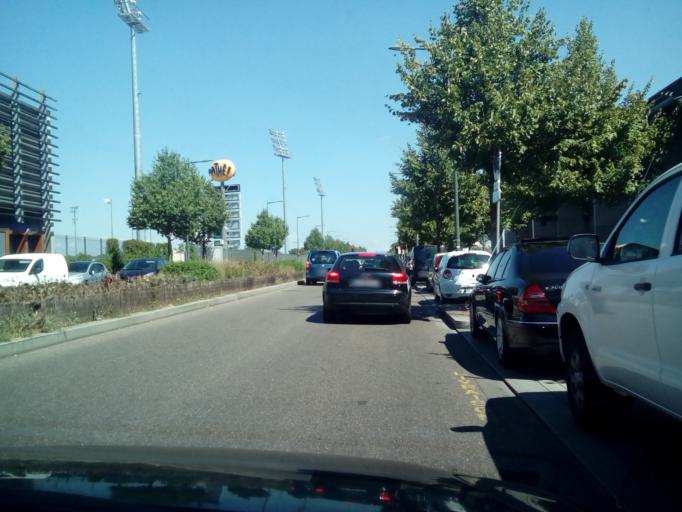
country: FR
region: Rhone-Alpes
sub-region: Departement du Rhone
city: Vaulx-en-Velin
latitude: 45.7650
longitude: 4.9222
